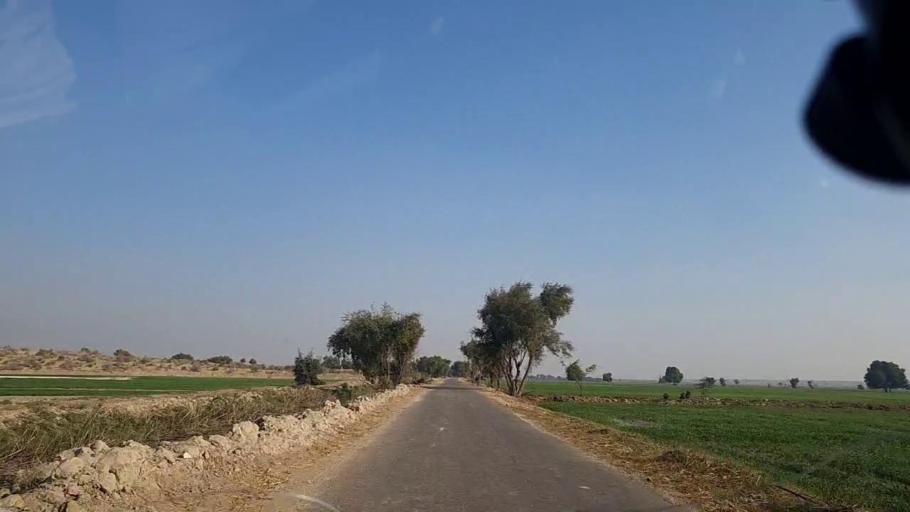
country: PK
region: Sindh
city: Khanpur
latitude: 27.6813
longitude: 69.5545
